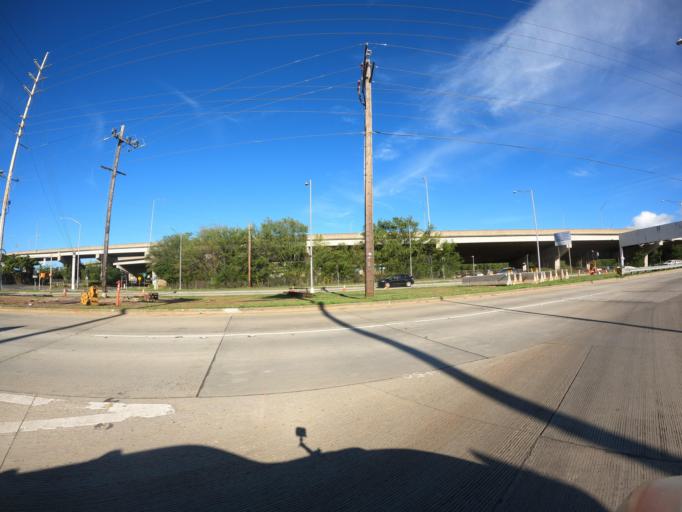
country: US
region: Hawaii
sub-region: Honolulu County
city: Honolulu
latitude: 21.3338
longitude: -157.8891
